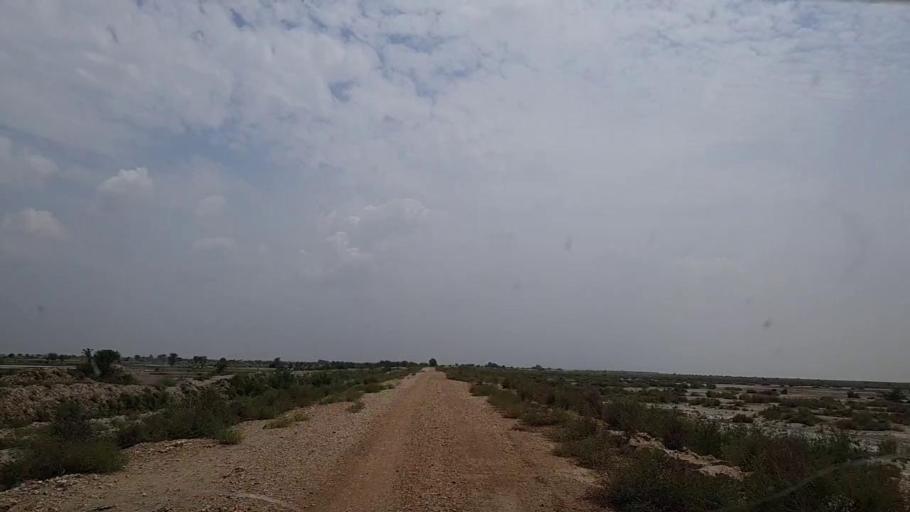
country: PK
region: Sindh
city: Phulji
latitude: 26.8369
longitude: 67.6178
